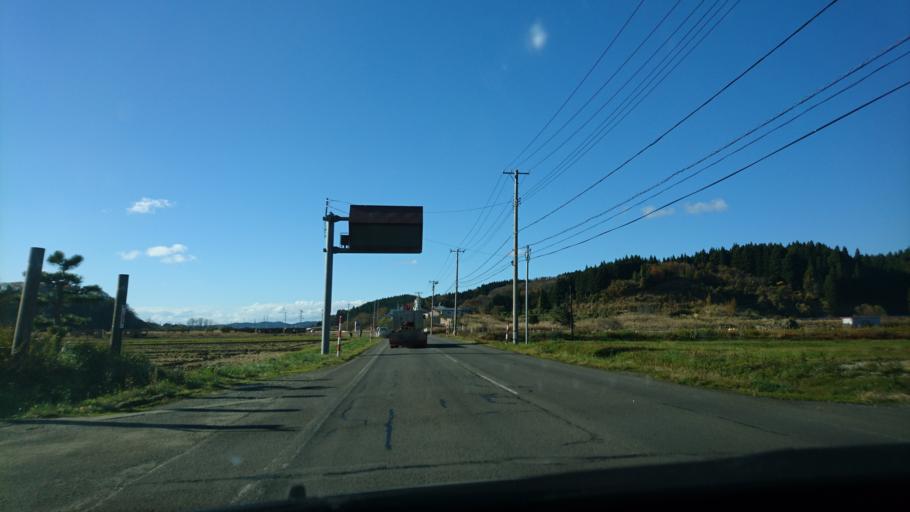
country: JP
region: Akita
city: Akita
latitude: 39.3541
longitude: 140.0946
